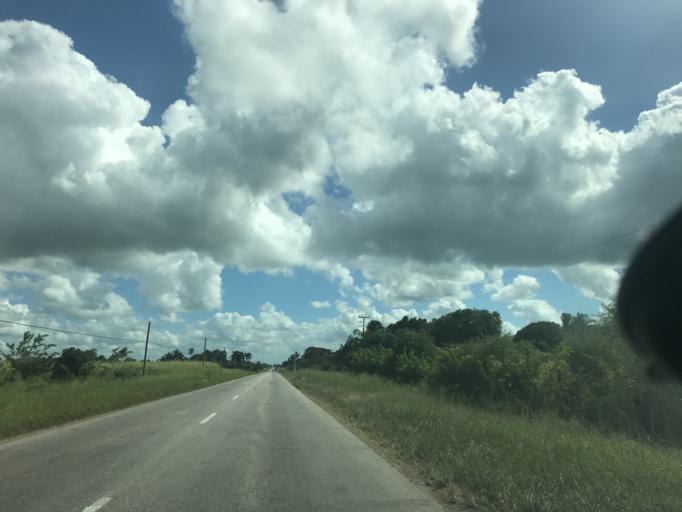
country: CU
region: Camaguey
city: Florida
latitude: 21.4834
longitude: -78.1823
